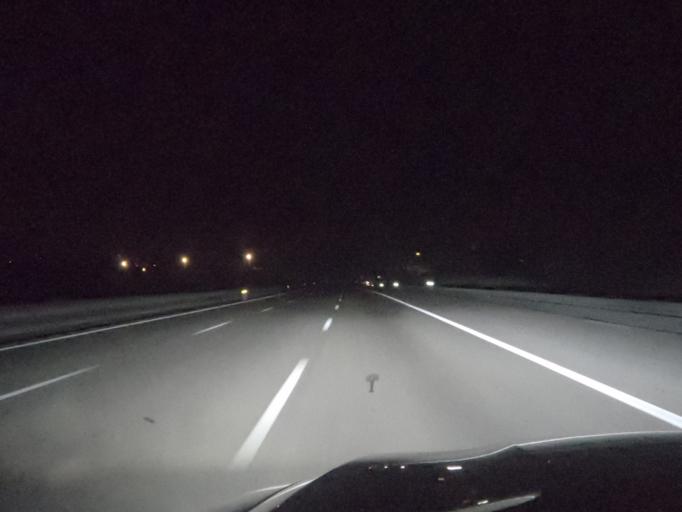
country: PT
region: Santarem
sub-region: Alcanena
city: Alcanena
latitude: 39.4056
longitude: -8.6371
